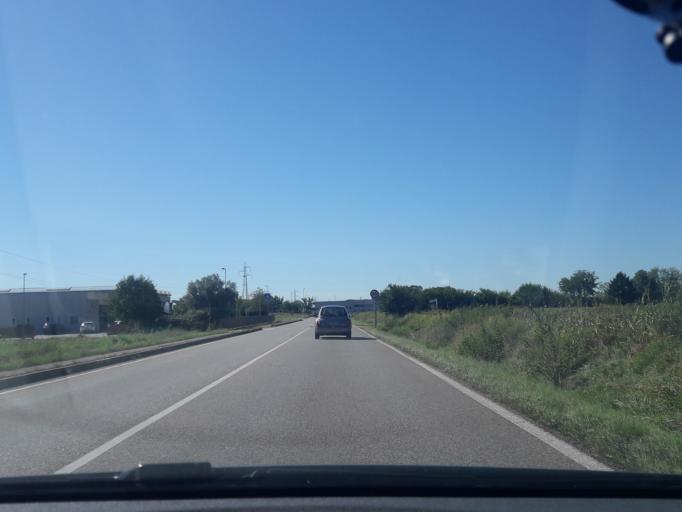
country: IT
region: Friuli Venezia Giulia
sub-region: Provincia di Udine
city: Pradamano
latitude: 46.0291
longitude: 13.2834
